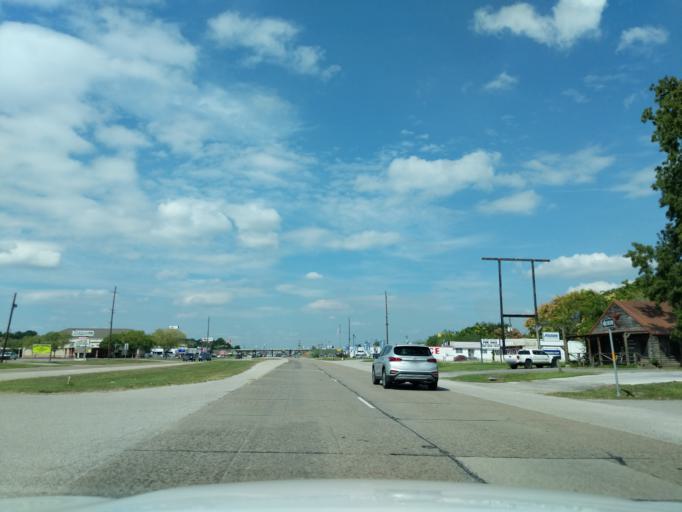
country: US
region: Texas
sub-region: Chambers County
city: Winnie
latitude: 29.8224
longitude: -94.3840
